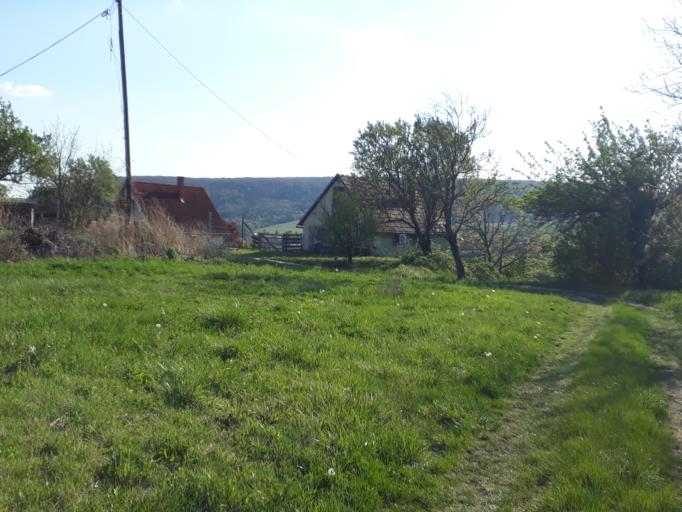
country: HU
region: Veszprem
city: Zanka
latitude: 46.9166
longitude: 17.6815
